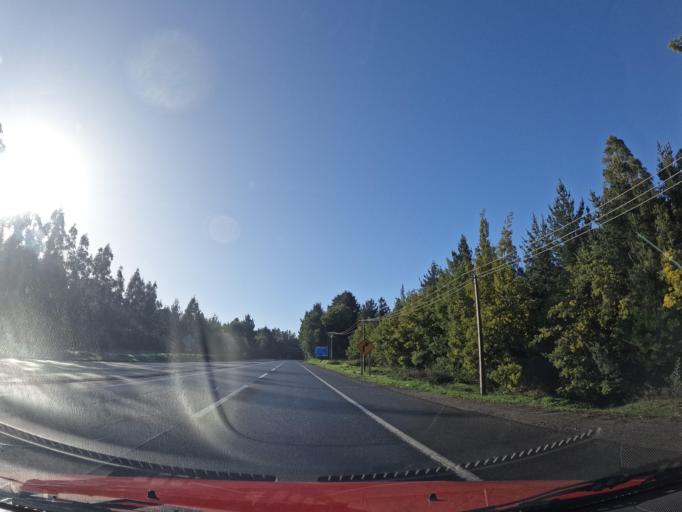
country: CL
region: Biobio
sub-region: Provincia de Concepcion
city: Penco
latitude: -36.7593
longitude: -72.9679
